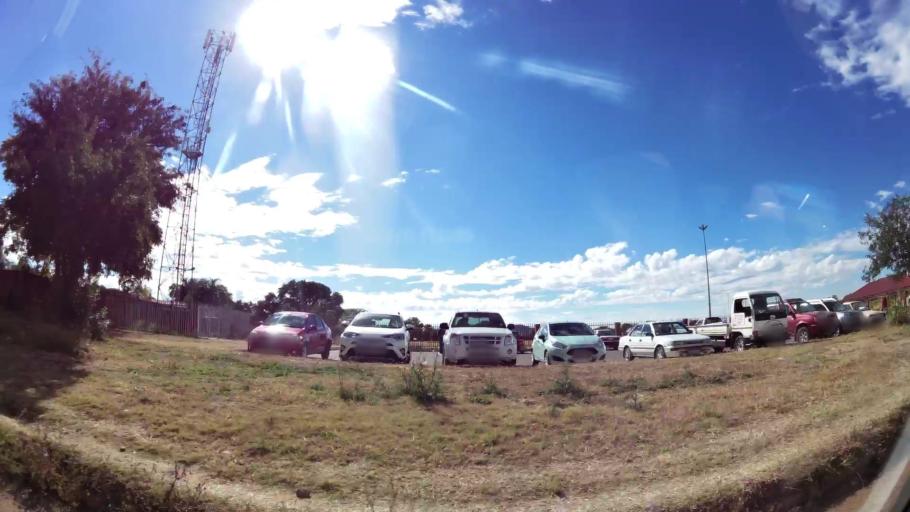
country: ZA
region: Limpopo
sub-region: Waterberg District Municipality
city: Bela-Bela
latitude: -24.8790
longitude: 28.2943
